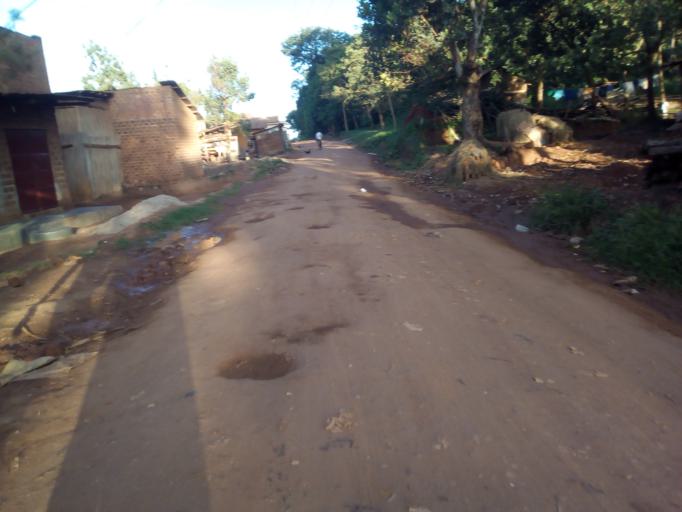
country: UG
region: Central Region
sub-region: Wakiso District
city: Kajansi
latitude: 0.2471
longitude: 32.5751
